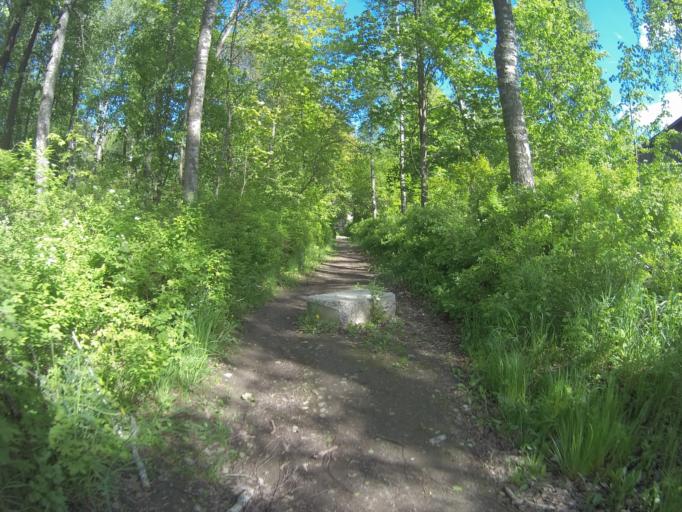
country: RU
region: Vladimir
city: Muromtsevo
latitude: 55.9305
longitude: 40.9010
